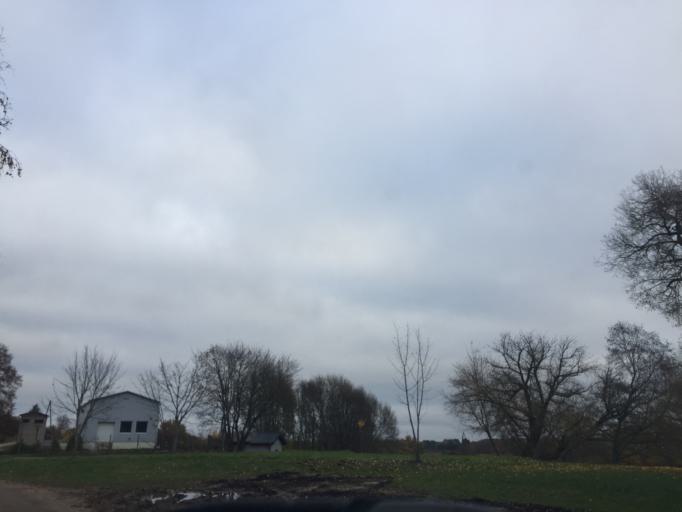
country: LV
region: Skrunda
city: Skrunda
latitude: 56.6749
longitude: 22.0259
